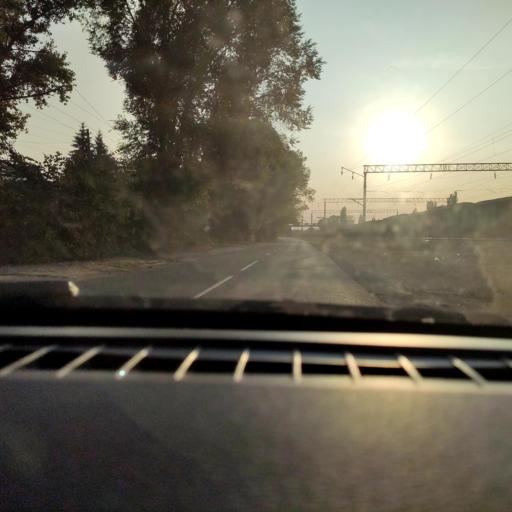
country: RU
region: Voronezj
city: Somovo
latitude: 51.7383
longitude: 39.3542
